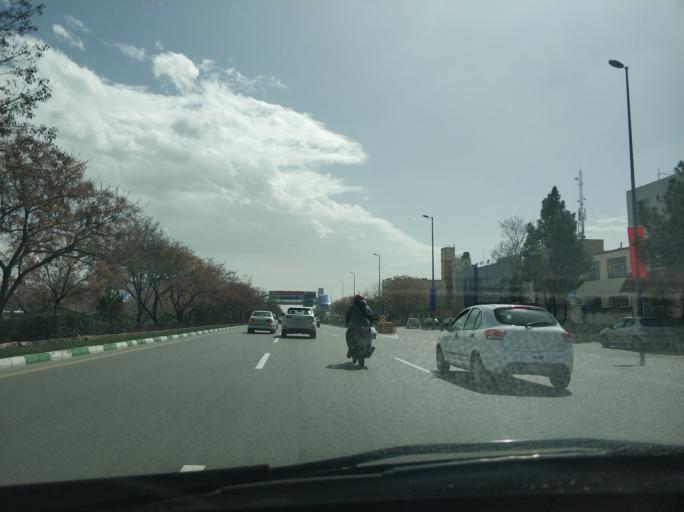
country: IR
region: Razavi Khorasan
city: Torqabeh
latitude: 36.3373
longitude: 59.4689
